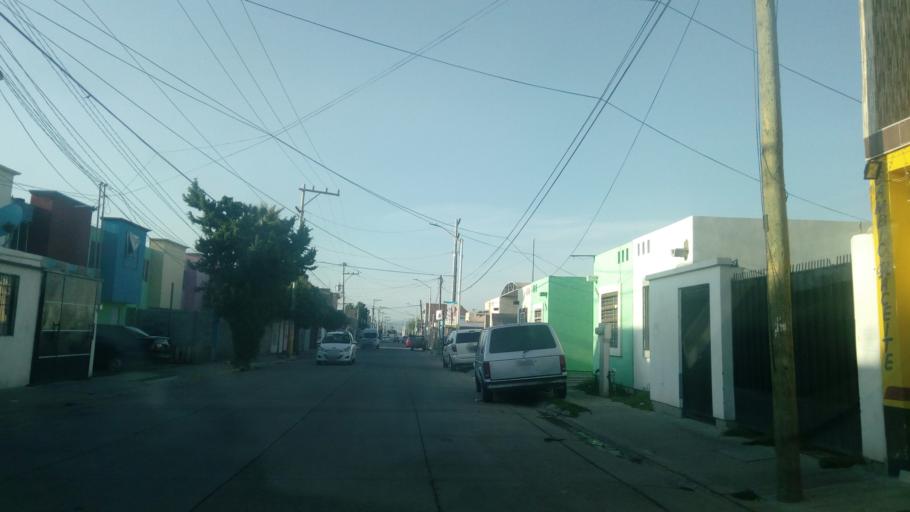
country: MX
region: Durango
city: Victoria de Durango
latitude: 24.0708
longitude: -104.5895
